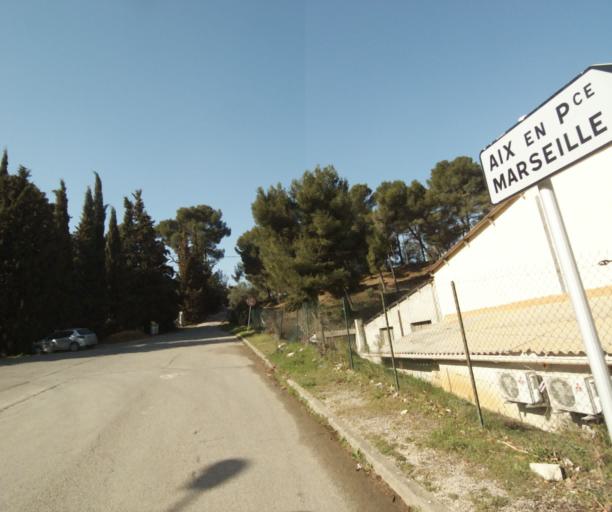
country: FR
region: Provence-Alpes-Cote d'Azur
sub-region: Departement des Bouches-du-Rhone
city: Gardanne
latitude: 43.4458
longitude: 5.4510
